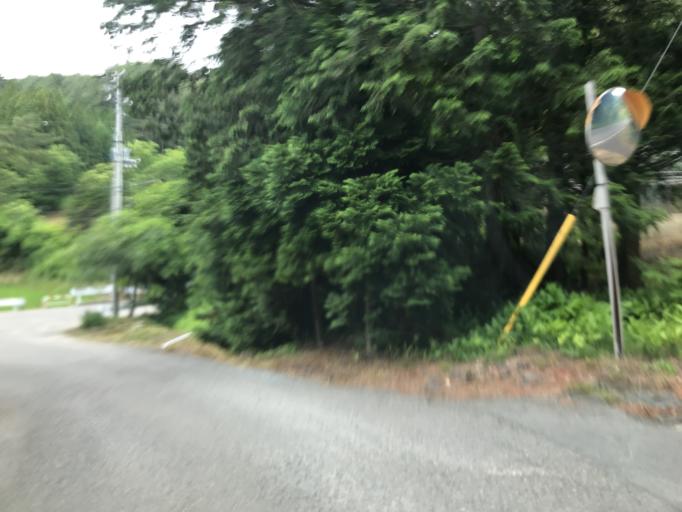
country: JP
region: Fukushima
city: Funehikimachi-funehiki
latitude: 37.4134
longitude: 140.7018
